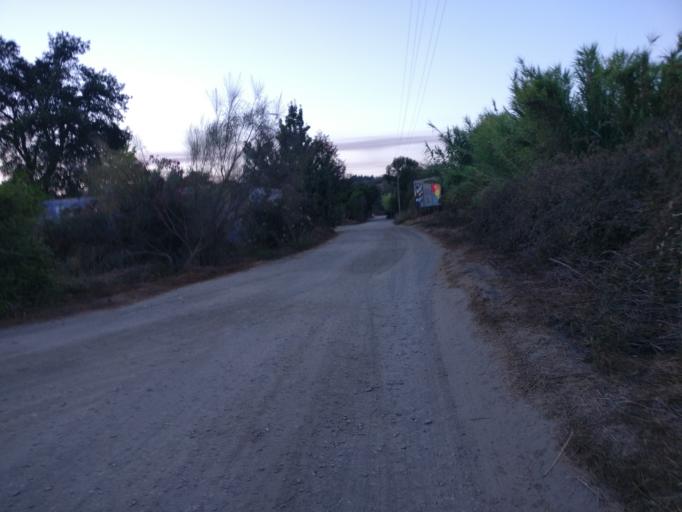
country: PT
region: Beja
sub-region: Odemira
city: Odemira
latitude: 37.7156
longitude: -8.5168
